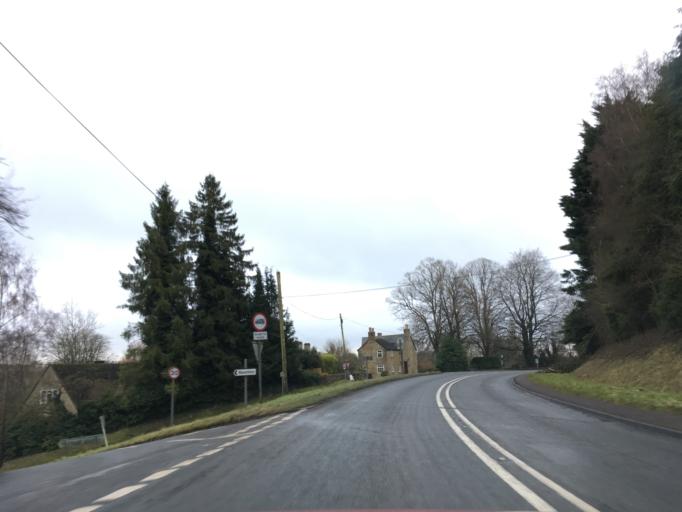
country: GB
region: England
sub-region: Gloucestershire
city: Cirencester
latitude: 51.7383
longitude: -1.9699
